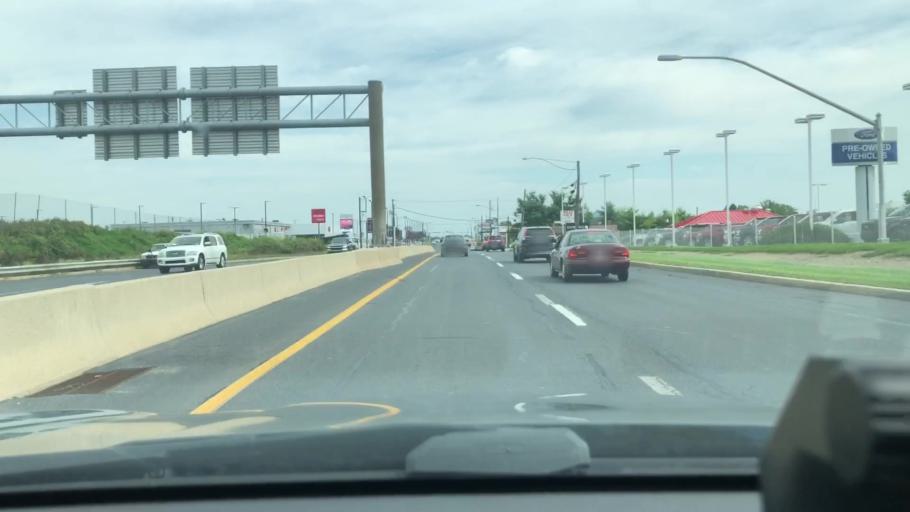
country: US
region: Pennsylvania
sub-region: Lehigh County
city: Emmaus
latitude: 40.5677
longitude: -75.4831
